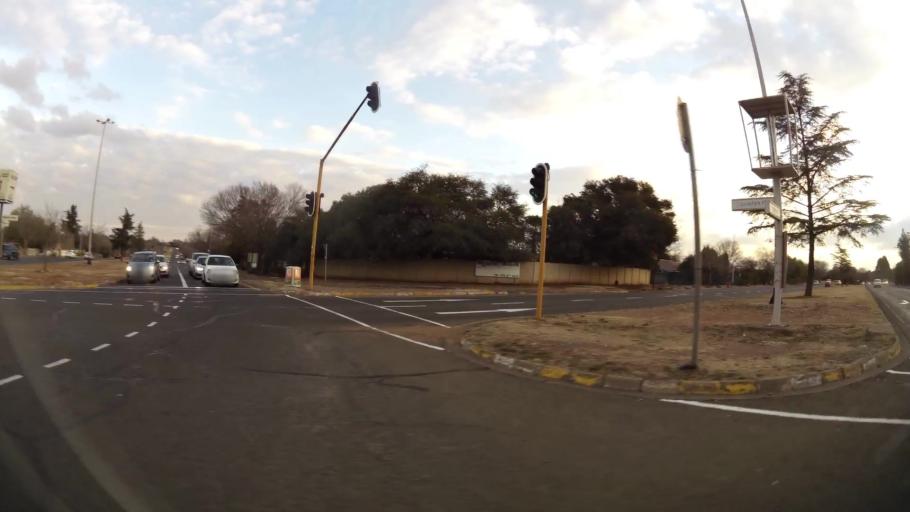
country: ZA
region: Orange Free State
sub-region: Mangaung Metropolitan Municipality
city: Bloemfontein
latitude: -29.1451
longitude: 26.1796
